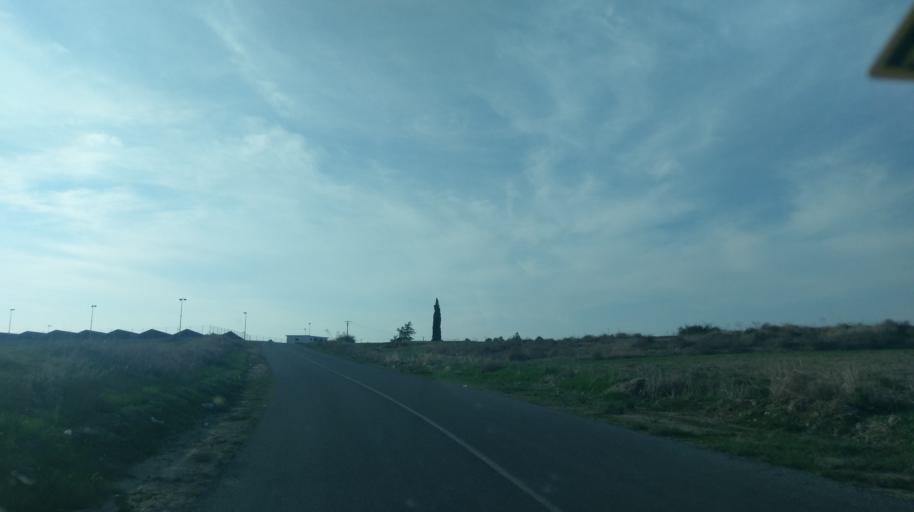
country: CY
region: Ammochostos
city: Achna
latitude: 35.1049
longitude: 33.7665
